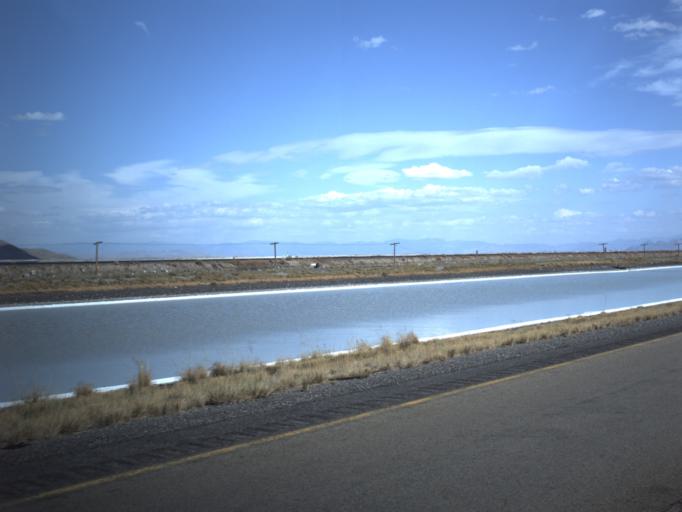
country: US
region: Utah
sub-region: Tooele County
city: Grantsville
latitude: 40.7309
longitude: -112.5926
